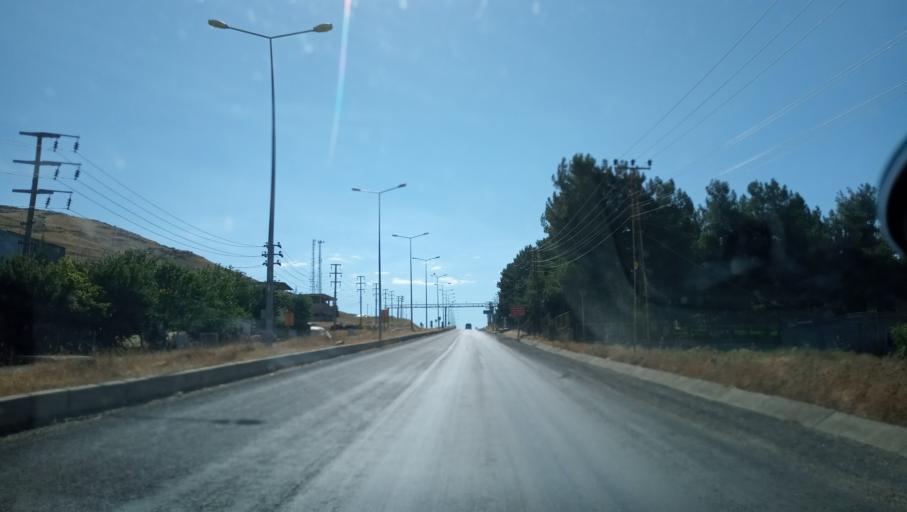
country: TR
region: Diyarbakir
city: Silvan
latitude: 38.1341
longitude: 41.0374
